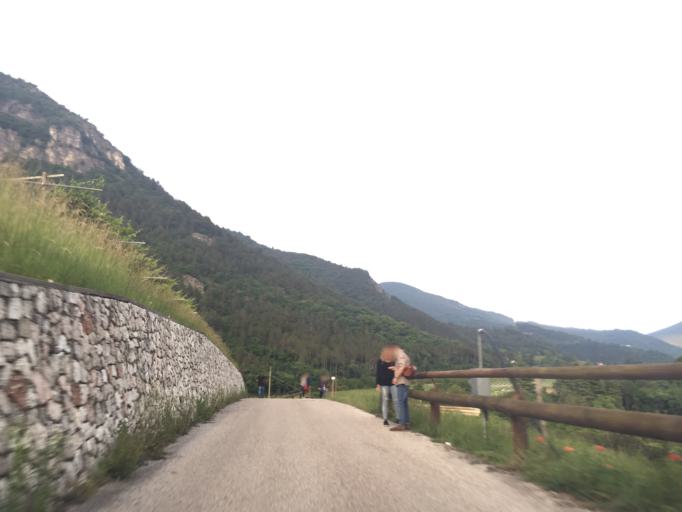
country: IT
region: Trentino-Alto Adige
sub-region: Provincia di Trento
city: Besenello
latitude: 45.9309
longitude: 11.1129
